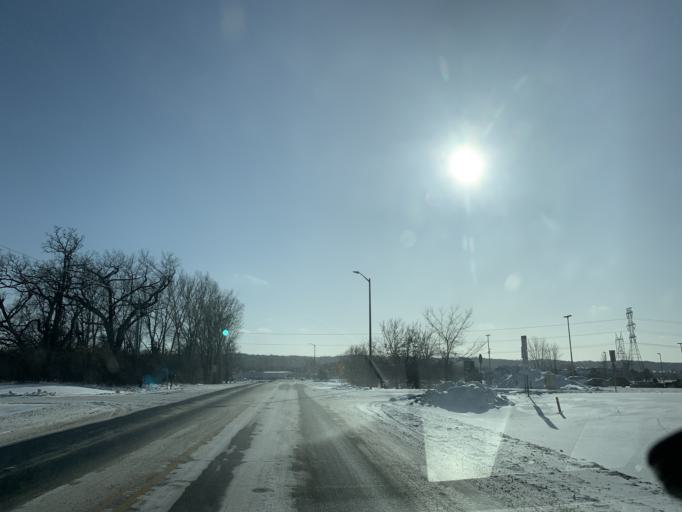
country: US
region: Minnesota
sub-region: Scott County
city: Prior Lake
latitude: 44.7807
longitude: -93.4070
